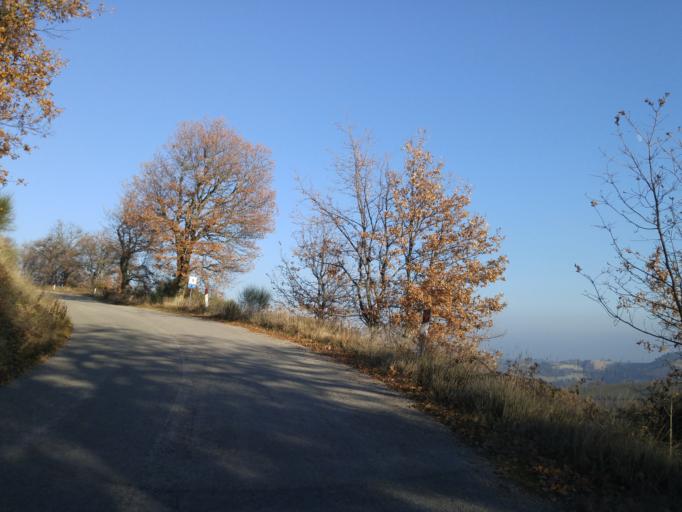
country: IT
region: The Marches
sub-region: Provincia di Pesaro e Urbino
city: Montefelcino
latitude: 43.7625
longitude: 12.8264
